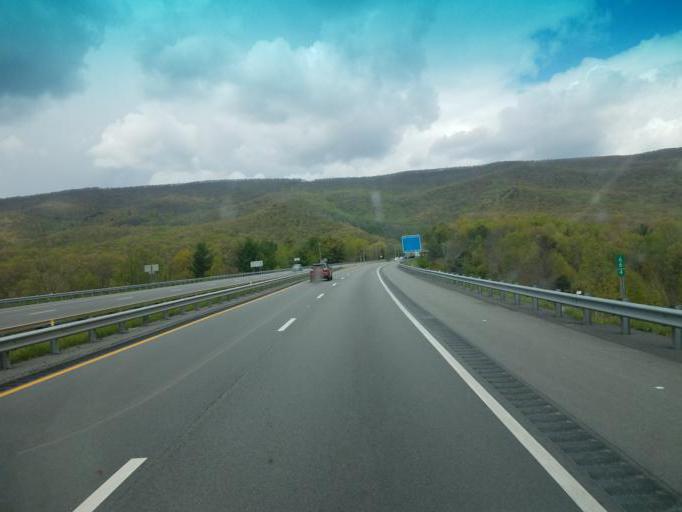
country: US
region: West Virginia
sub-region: Mercer County
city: Bluefield
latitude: 37.2583
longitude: -81.1202
